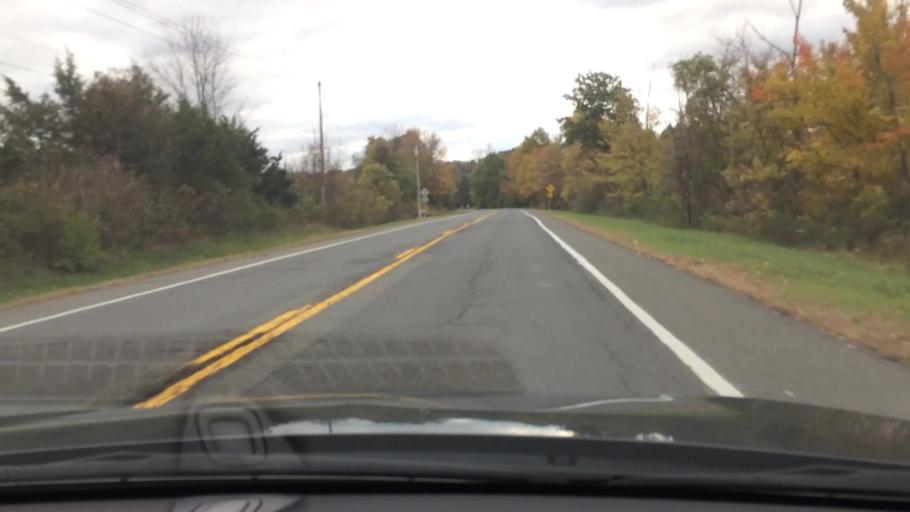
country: US
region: New York
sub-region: Columbia County
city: Oakdale
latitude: 42.1501
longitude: -73.7458
